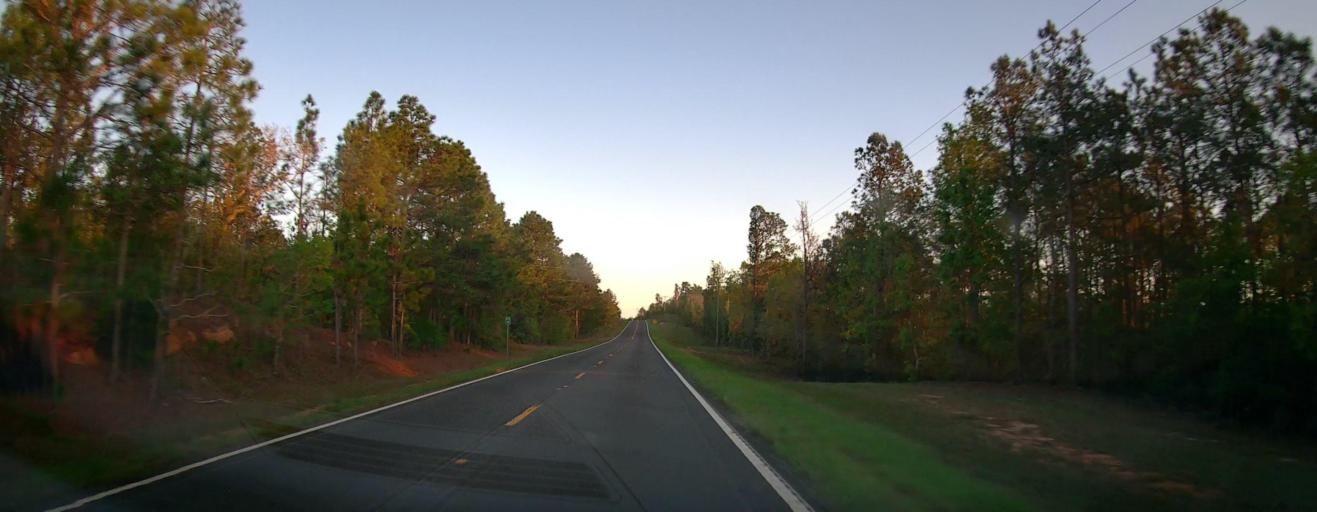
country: US
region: Georgia
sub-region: Marion County
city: Buena Vista
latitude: 32.4084
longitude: -84.5829
